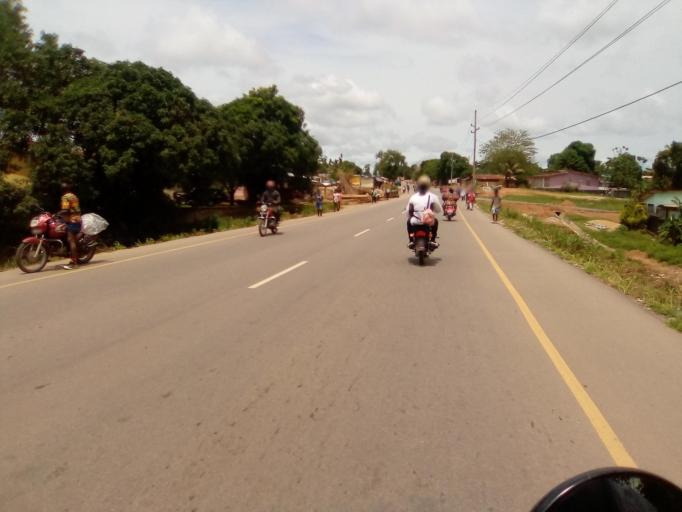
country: SL
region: Southern Province
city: Bo
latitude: 7.9367
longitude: -11.7258
